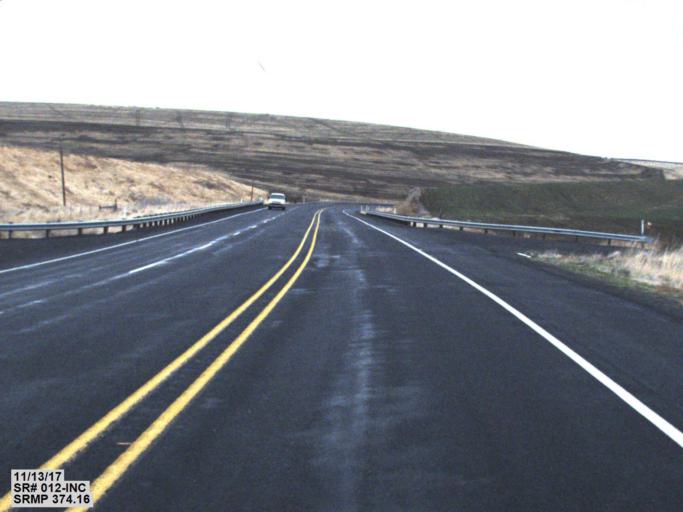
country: US
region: Washington
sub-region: Columbia County
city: Dayton
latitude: 46.4019
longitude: -117.9356
